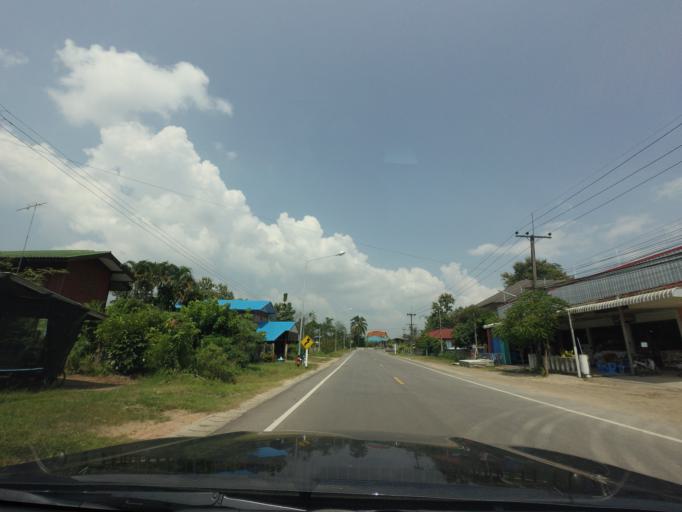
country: TH
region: Nan
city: Santi Suk
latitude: 18.9364
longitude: 100.9267
